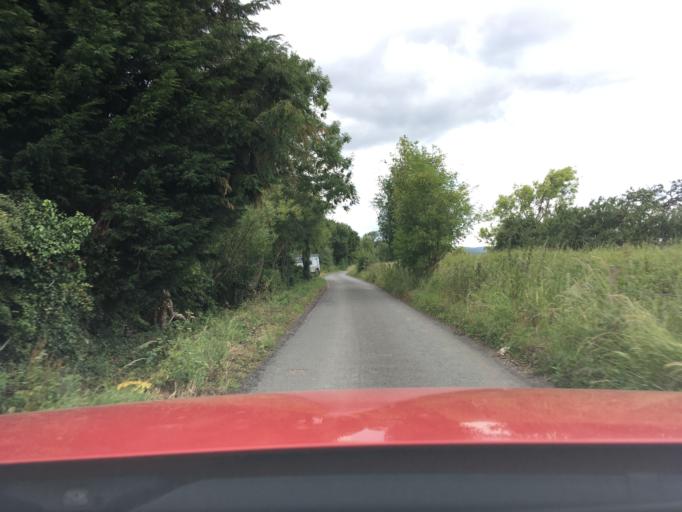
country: GB
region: England
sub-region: Gloucestershire
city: Stonehouse
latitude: 51.7934
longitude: -2.3776
